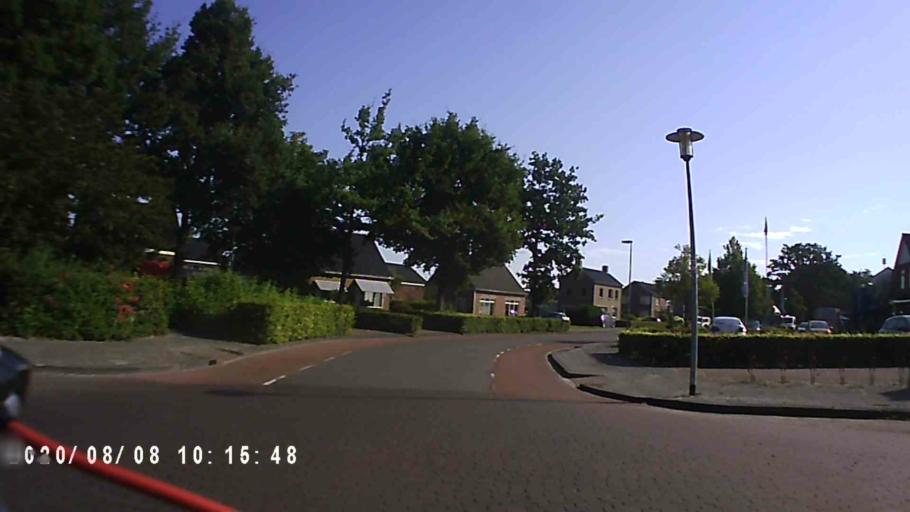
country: NL
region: Groningen
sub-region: Gemeente Leek
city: Leek
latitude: 53.1313
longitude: 6.3983
